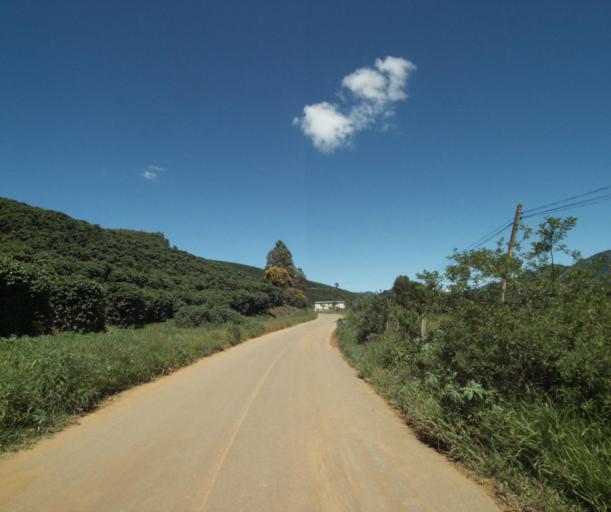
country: BR
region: Minas Gerais
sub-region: Espera Feliz
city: Espera Feliz
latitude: -20.5606
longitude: -41.8229
